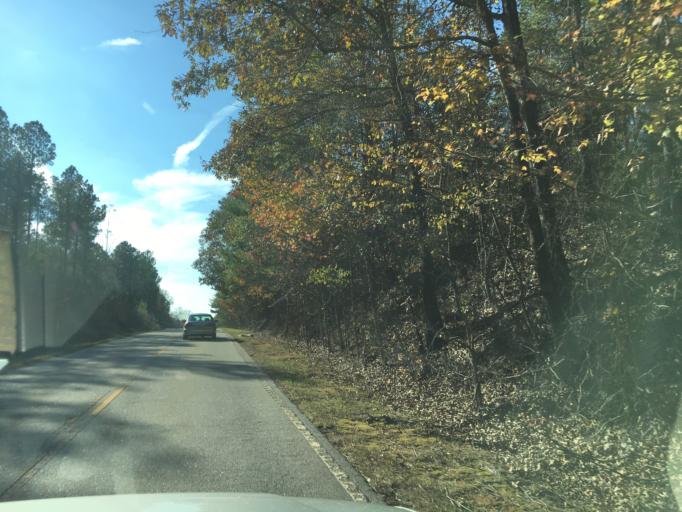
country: US
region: South Carolina
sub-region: Anderson County
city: Iva
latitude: 34.3320
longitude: -82.7764
